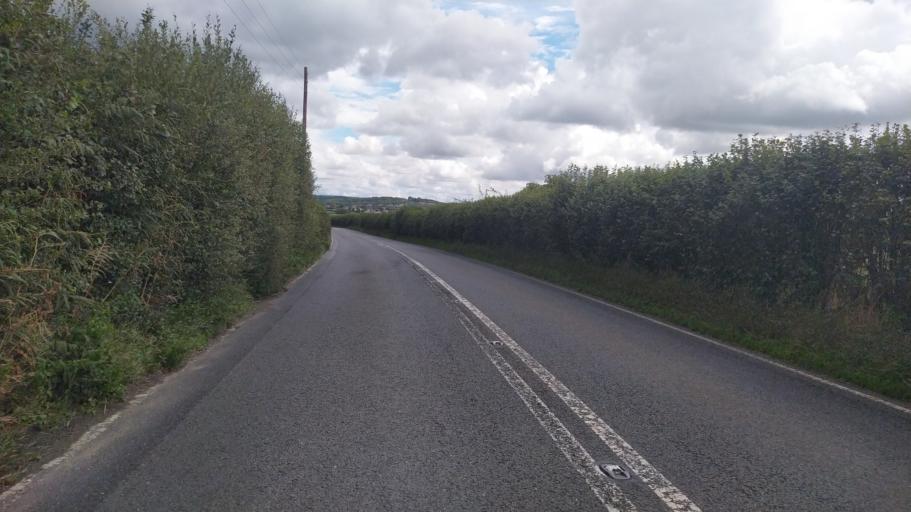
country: GB
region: England
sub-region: Dorset
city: Sturminster Newton
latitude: 50.9184
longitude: -2.3385
